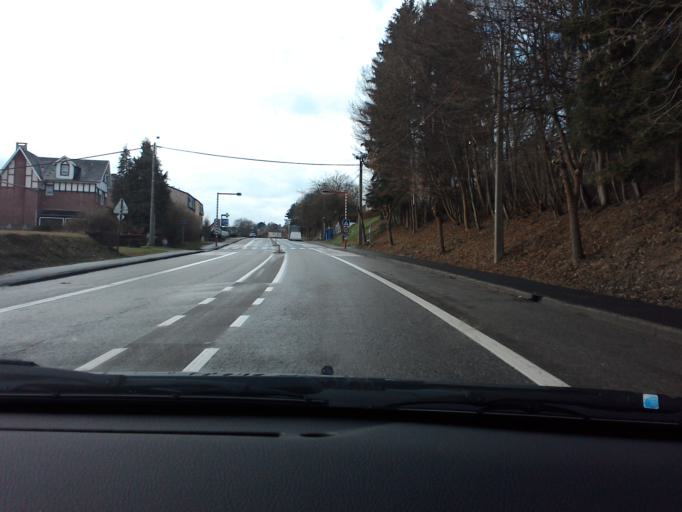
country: BE
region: Wallonia
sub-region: Province de Liege
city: Stavelot
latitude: 50.3948
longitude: 5.9274
